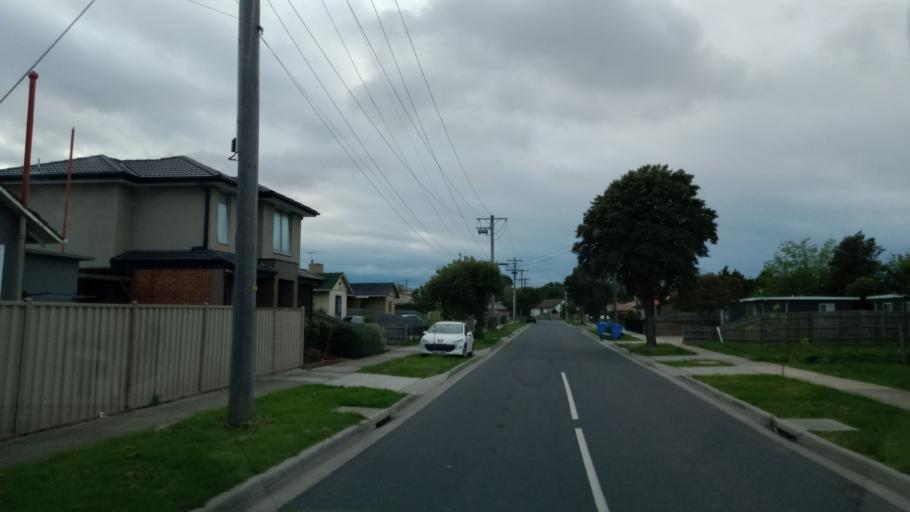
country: AU
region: Victoria
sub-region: Casey
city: Doveton
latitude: -37.9969
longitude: 145.2378
